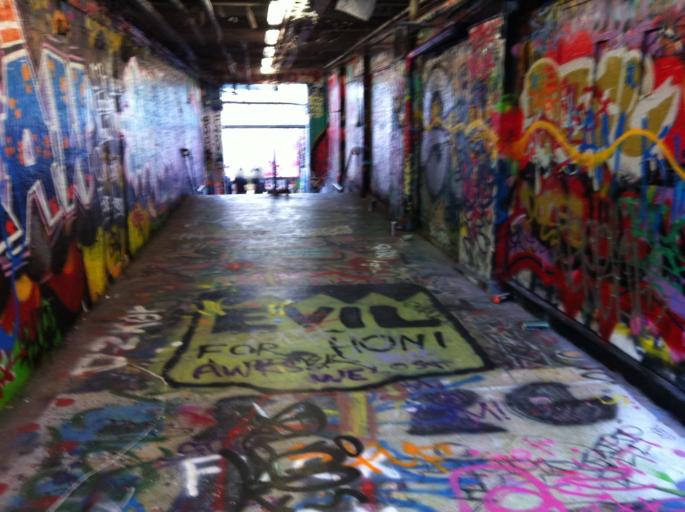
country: AU
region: New South Wales
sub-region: City of Sydney
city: Darlington
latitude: -33.8856
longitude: 151.1875
